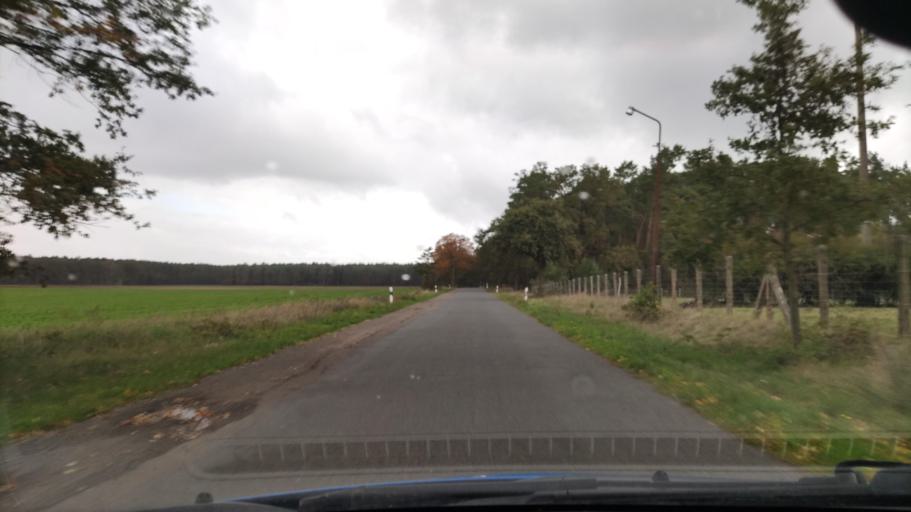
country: DE
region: Saxony-Anhalt
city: Luftkurort Arendsee
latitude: 52.9628
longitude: 11.5473
